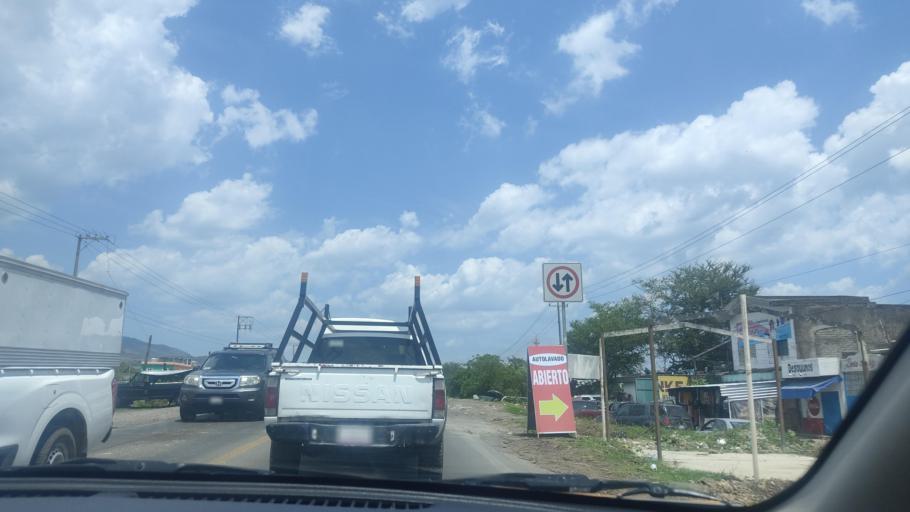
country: MX
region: Nayarit
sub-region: Tepic
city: La Corregidora
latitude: 21.4478
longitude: -104.8128
